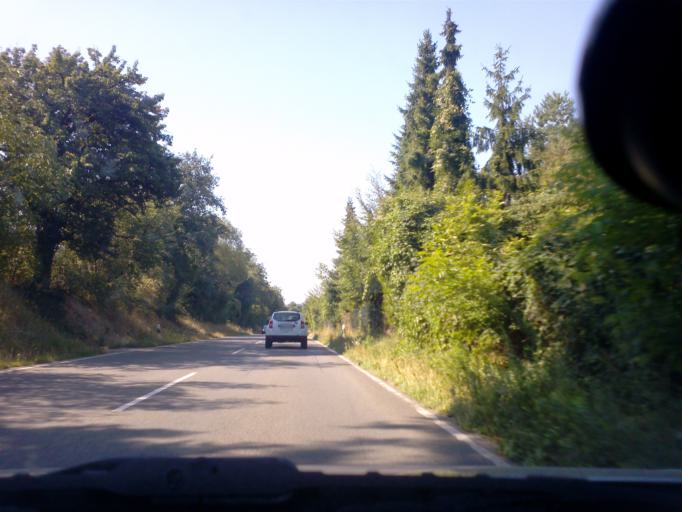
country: DE
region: Baden-Wuerttemberg
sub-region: Karlsruhe Region
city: Weingarten
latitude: 49.0615
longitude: 8.5360
